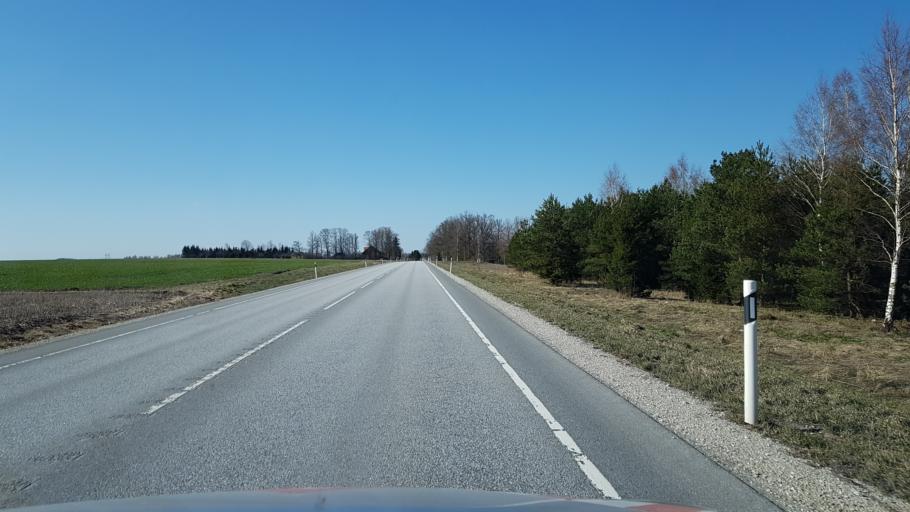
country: EE
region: Tartu
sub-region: Tartu linn
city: Tartu
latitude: 58.5417
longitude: 26.7619
